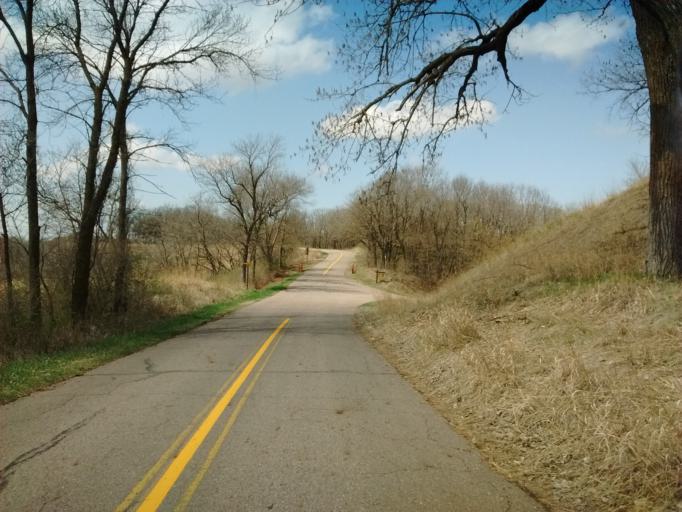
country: US
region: South Dakota
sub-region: Union County
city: North Sioux City
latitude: 42.5542
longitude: -96.4625
